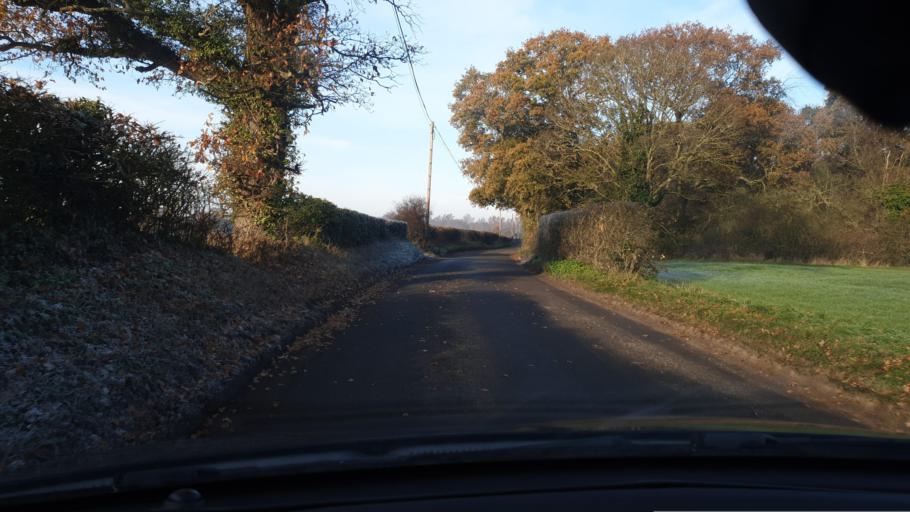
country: GB
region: England
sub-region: Essex
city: Mistley
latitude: 51.9744
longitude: 1.1210
